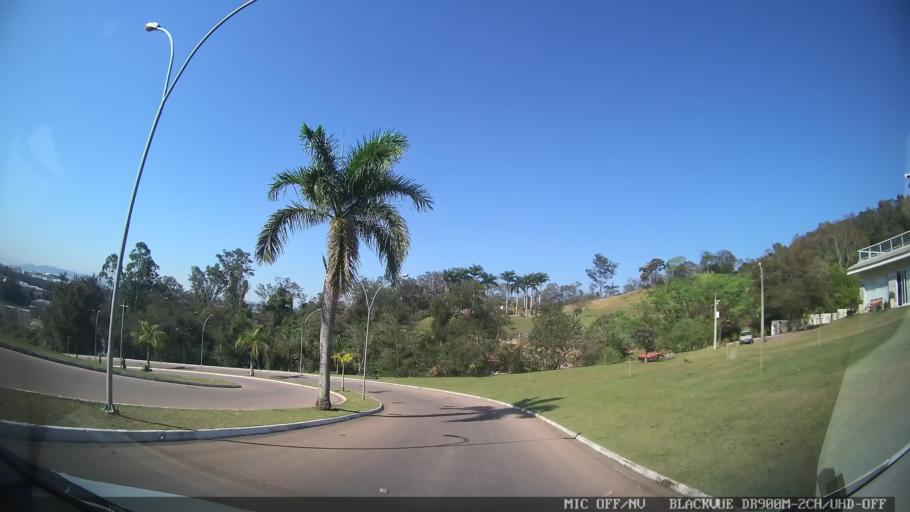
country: BR
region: Sao Paulo
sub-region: Itupeva
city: Itupeva
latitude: -23.1445
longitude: -47.0504
